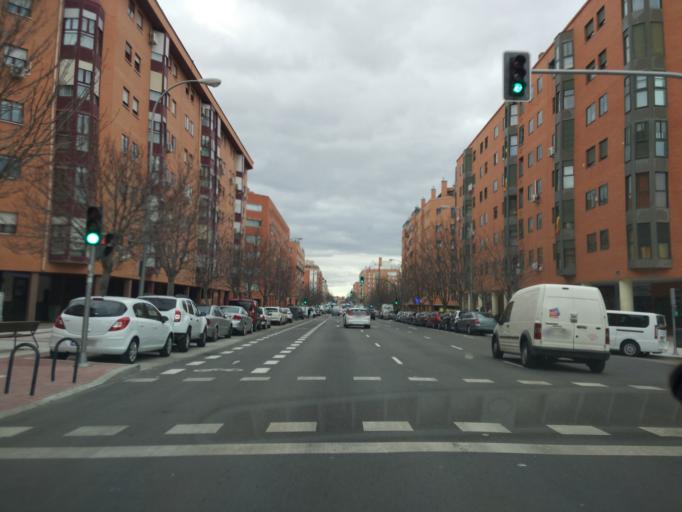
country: ES
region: Madrid
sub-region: Provincia de Madrid
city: San Blas
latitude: 40.4202
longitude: -3.6142
